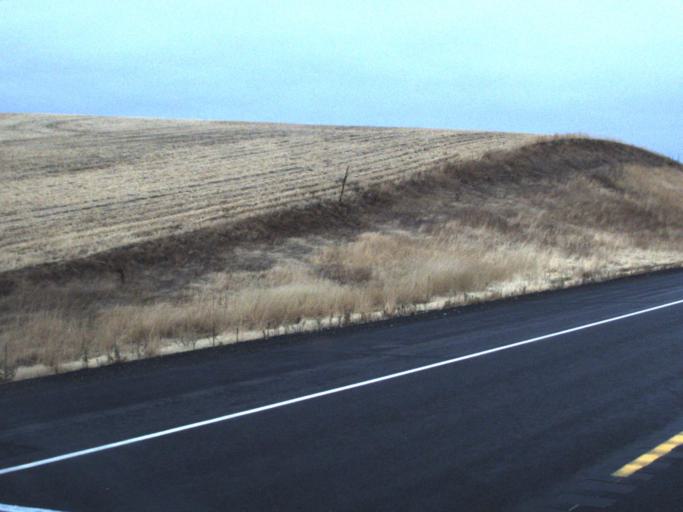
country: US
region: Washington
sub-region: Spokane County
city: Cheney
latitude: 47.3991
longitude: -117.3915
